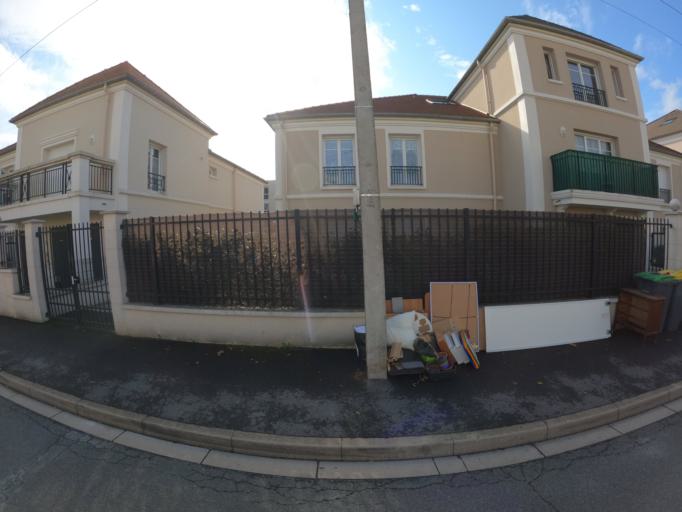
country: FR
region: Ile-de-France
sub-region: Departement de Seine-et-Marne
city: Vaires-sur-Marne
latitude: 48.8767
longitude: 2.6358
